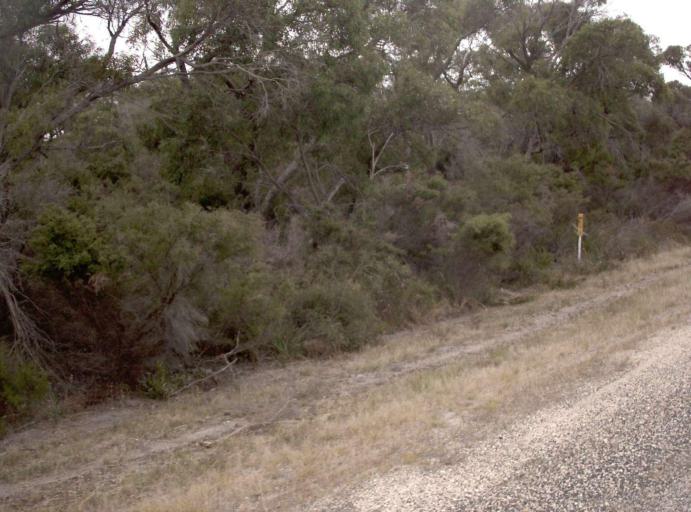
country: AU
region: Victoria
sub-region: East Gippsland
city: Bairnsdale
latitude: -38.1247
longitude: 147.4348
